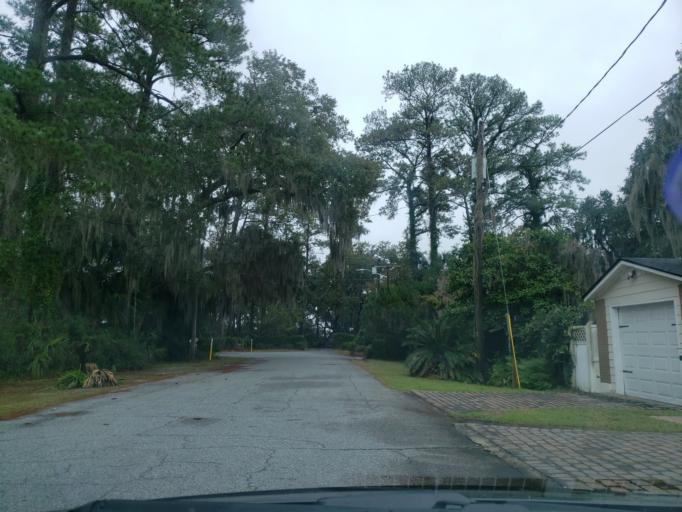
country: US
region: Georgia
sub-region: Chatham County
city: Georgetown
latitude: 31.9745
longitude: -81.1881
